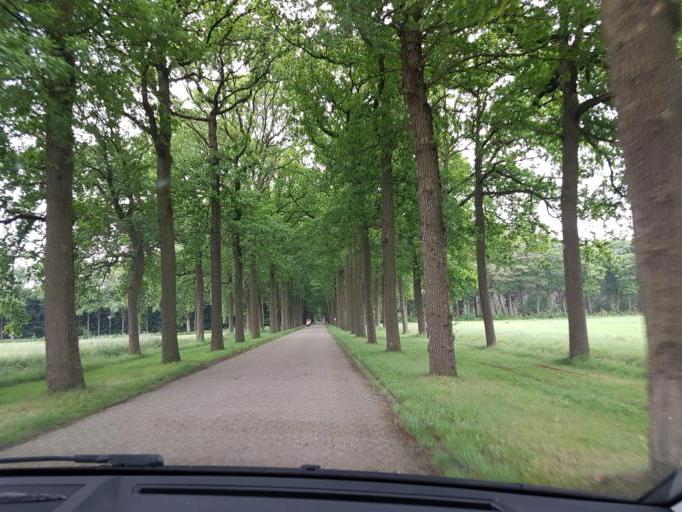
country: BE
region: Flanders
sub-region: Provincie Antwerpen
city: Merksplas
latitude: 51.3944
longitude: 4.8269
